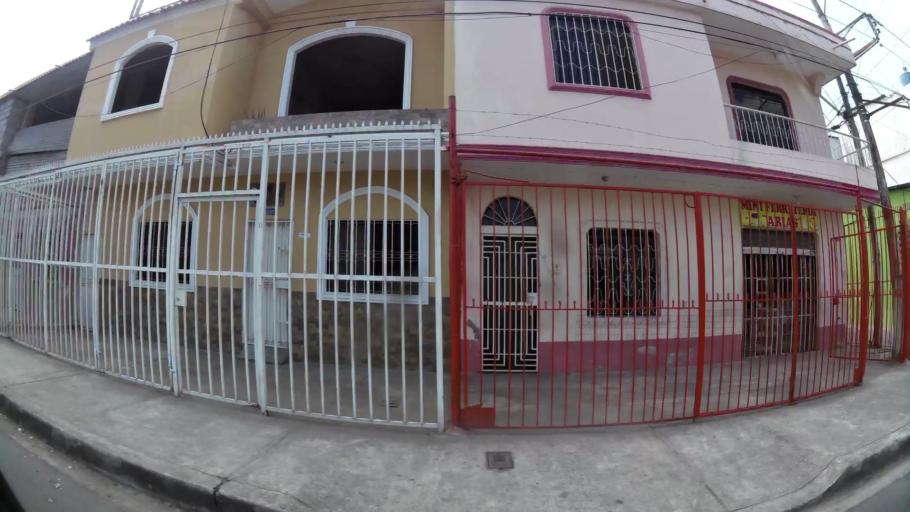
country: EC
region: Guayas
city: Guayaquil
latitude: -2.1255
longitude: -79.9278
